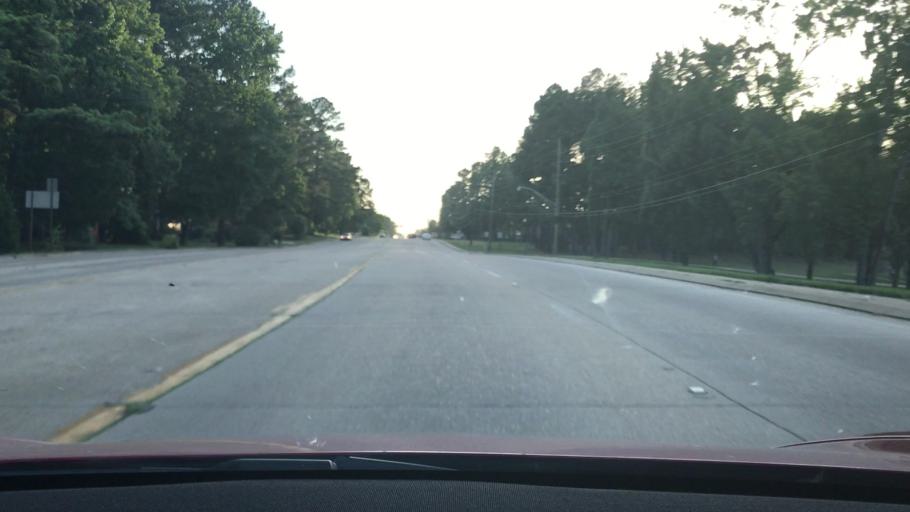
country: US
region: Louisiana
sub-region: Bossier Parish
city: Bossier City
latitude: 32.4021
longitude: -93.7852
